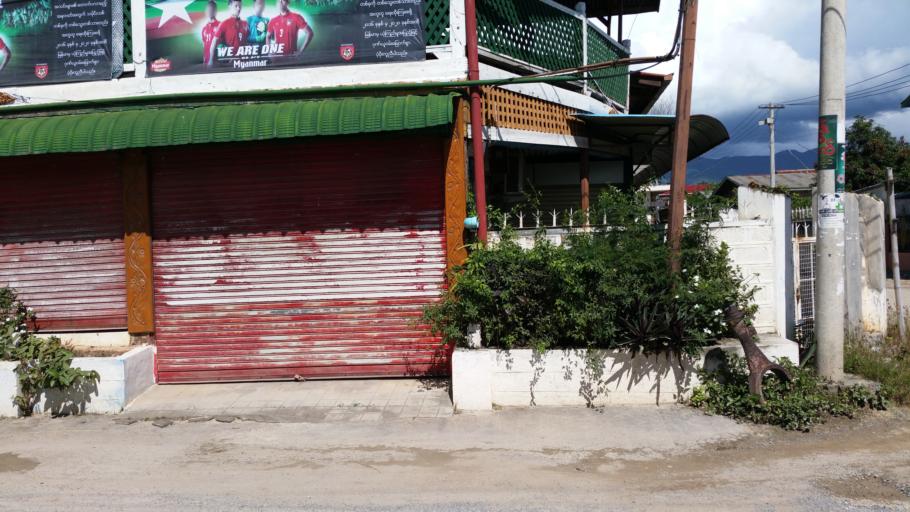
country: MM
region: Shan
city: Taunggyi
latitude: 20.6584
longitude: 96.9248
